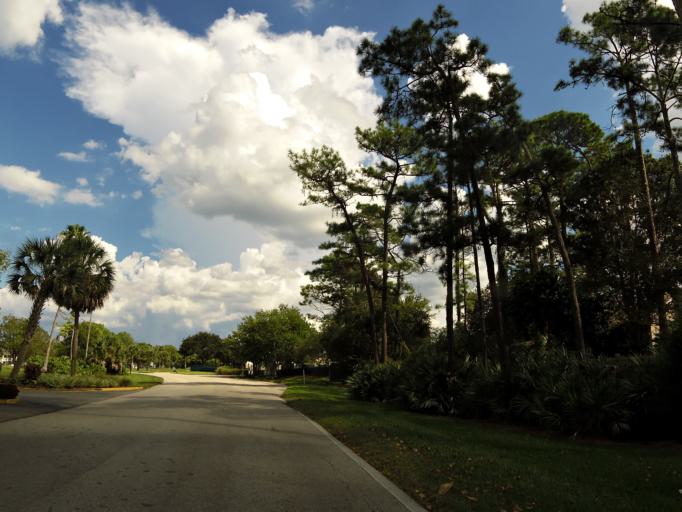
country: US
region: Florida
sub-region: Saint Johns County
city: Ponte Vedra Beach
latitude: 30.2511
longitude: -81.3991
